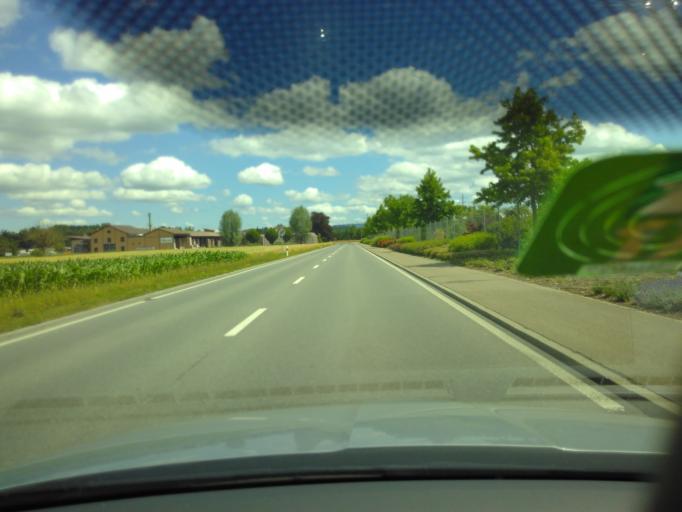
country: CH
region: Lucerne
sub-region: Lucerne-Land District
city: Root
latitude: 47.1282
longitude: 8.3937
